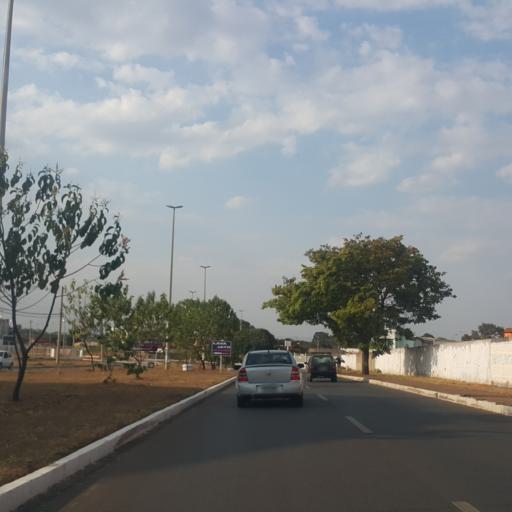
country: BR
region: Federal District
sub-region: Brasilia
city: Brasilia
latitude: -15.8688
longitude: -48.0237
